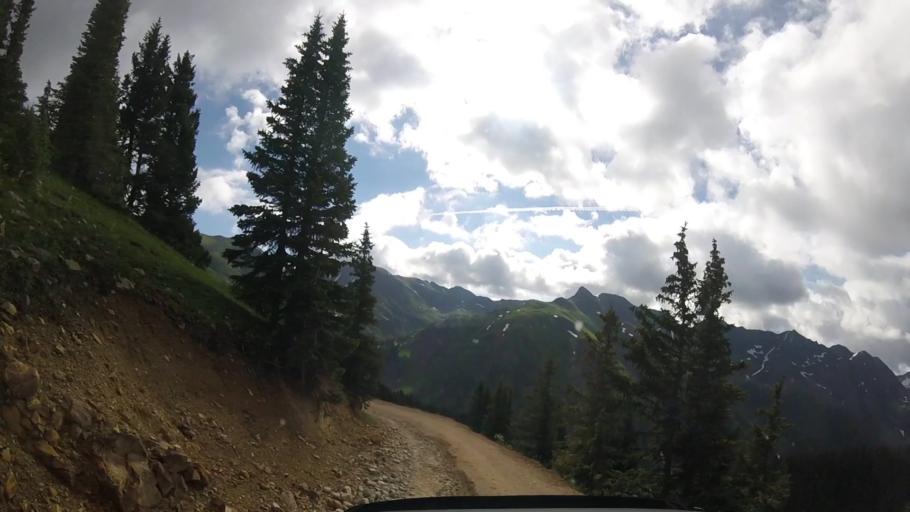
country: US
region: Colorado
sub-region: San Juan County
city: Silverton
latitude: 37.9058
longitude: -107.6559
